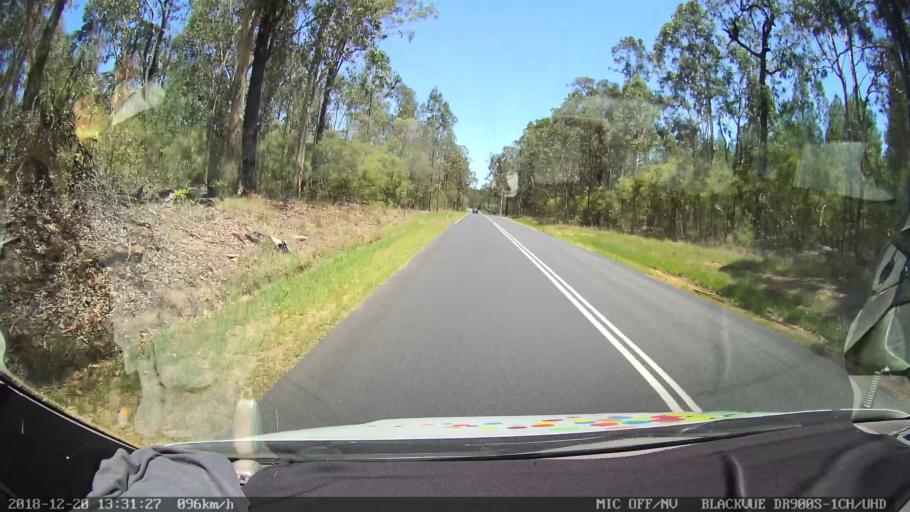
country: AU
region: New South Wales
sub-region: Clarence Valley
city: Gordon
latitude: -29.2181
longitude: 152.9889
